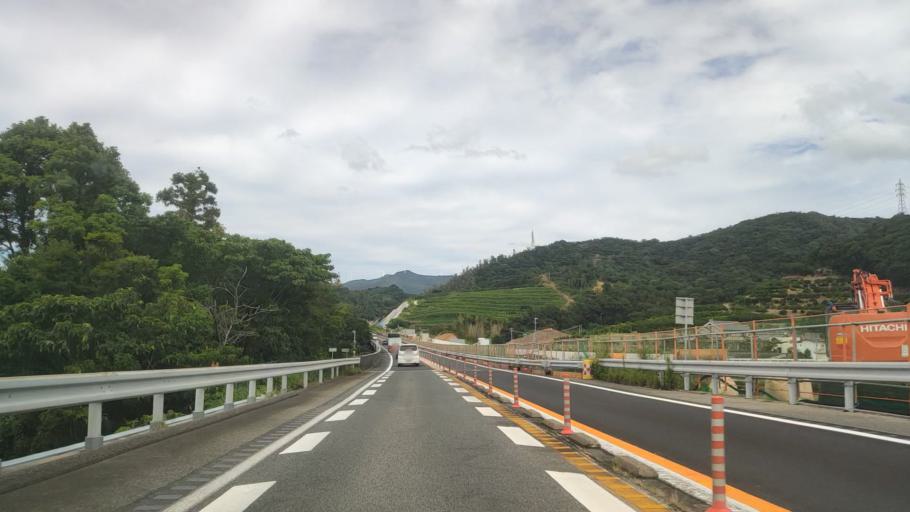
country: JP
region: Wakayama
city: Gobo
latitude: 33.9137
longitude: 135.1944
